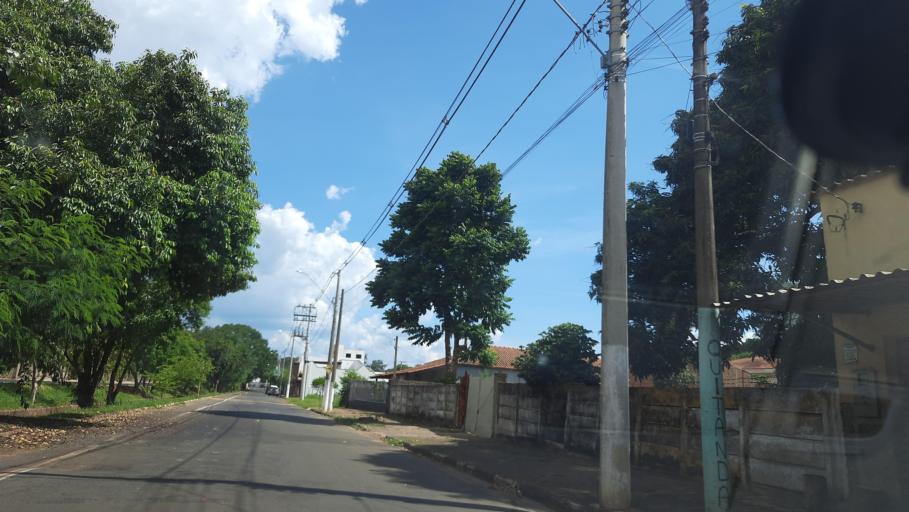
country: BR
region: Sao Paulo
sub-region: Casa Branca
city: Casa Branca
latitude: -21.7755
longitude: -47.0906
